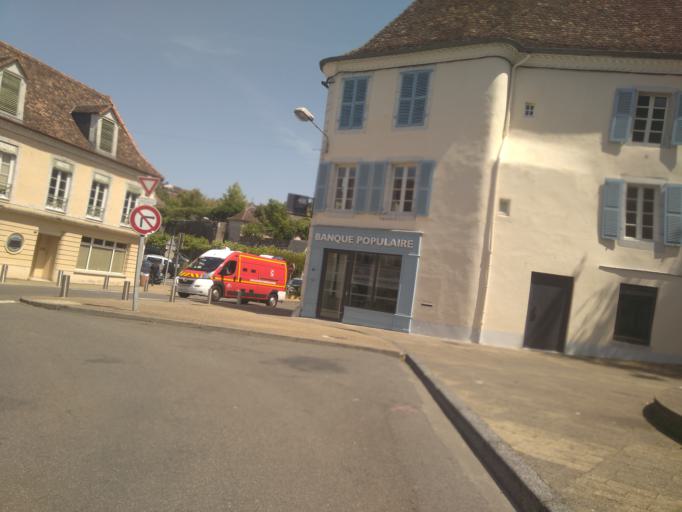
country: FR
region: Aquitaine
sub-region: Departement des Pyrenees-Atlantiques
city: Orthez
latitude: 43.4902
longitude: -0.7752
